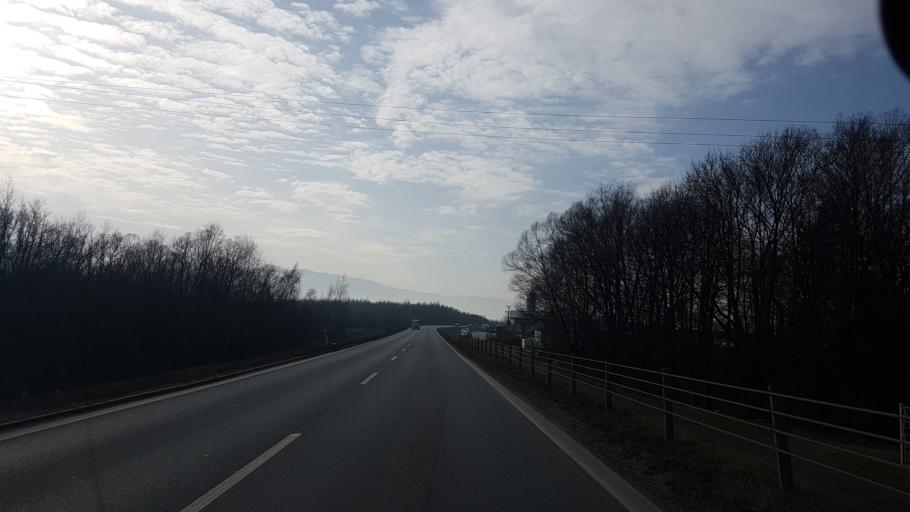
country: PL
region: Lesser Poland Voivodeship
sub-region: Powiat nowosadecki
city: Podegrodzie
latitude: 49.5767
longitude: 20.6094
